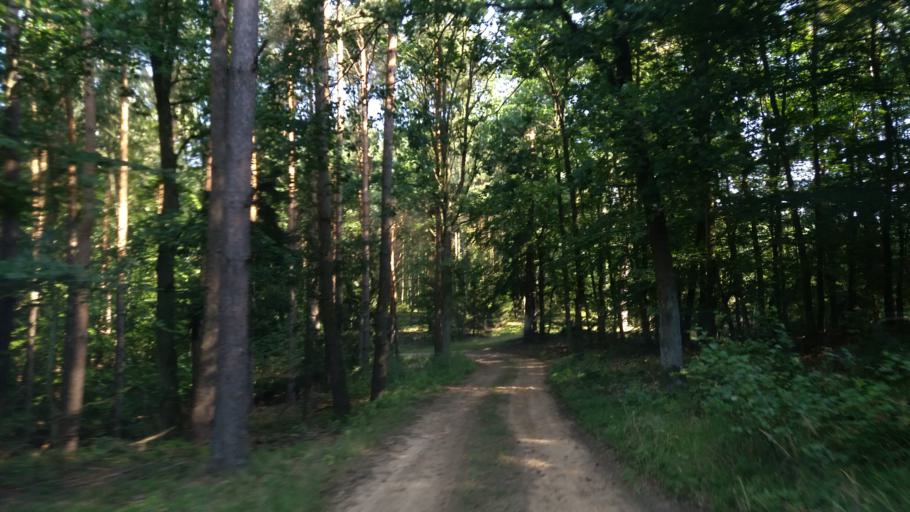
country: PL
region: West Pomeranian Voivodeship
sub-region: Powiat choszczenski
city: Pelczyce
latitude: 52.9732
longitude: 15.3581
